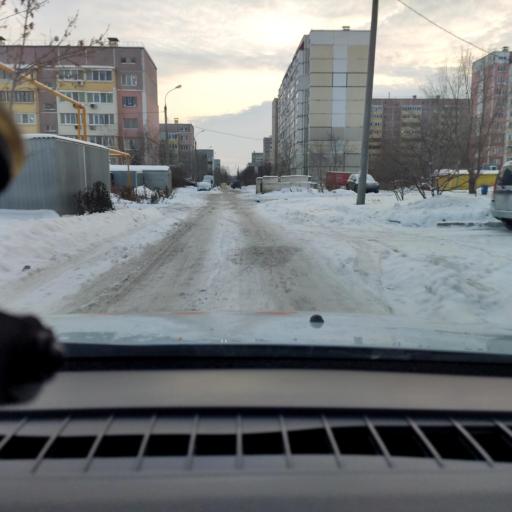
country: RU
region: Samara
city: Samara
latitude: 53.1102
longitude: 50.0853
